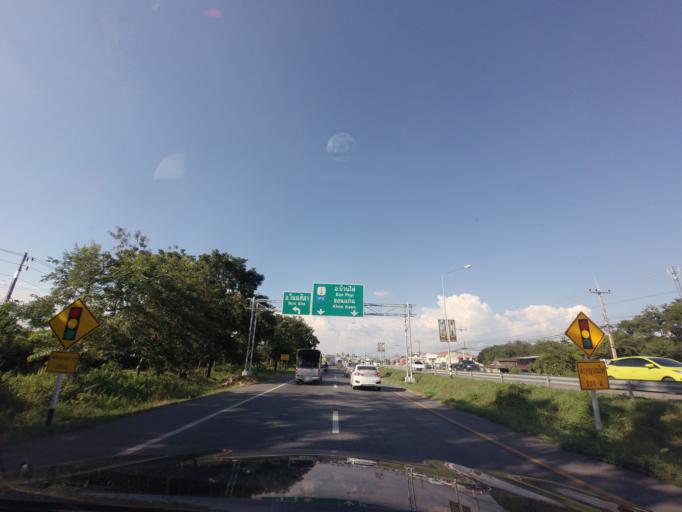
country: TH
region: Khon Kaen
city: Non Sila
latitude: 15.9642
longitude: 102.6907
